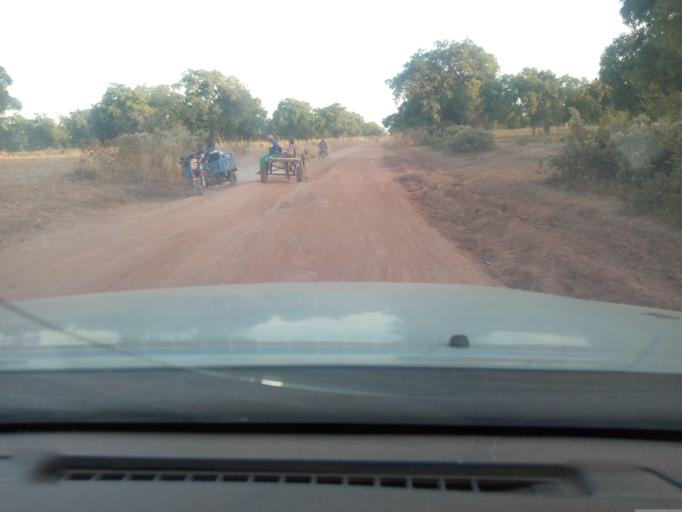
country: ML
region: Koulikoro
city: Dioila
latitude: 12.2102
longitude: -6.2011
